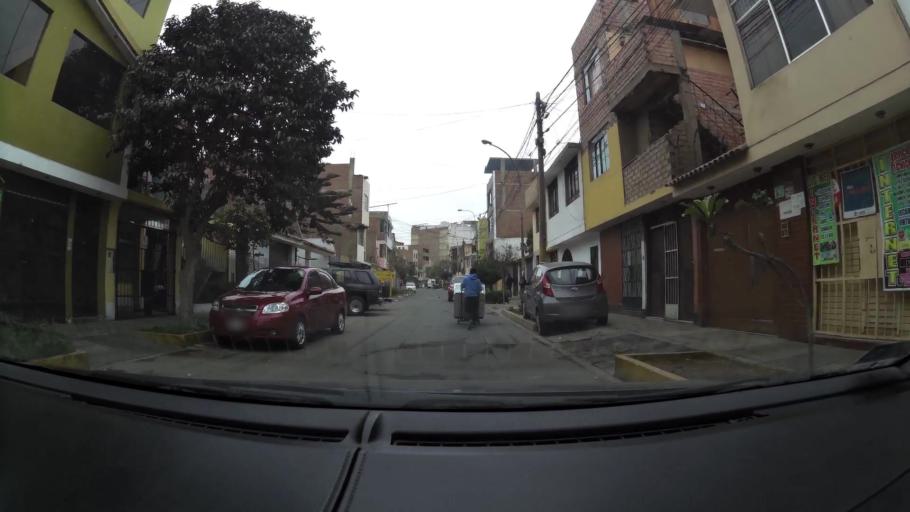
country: PE
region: Lima
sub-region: Lima
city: Independencia
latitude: -11.9618
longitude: -77.0747
